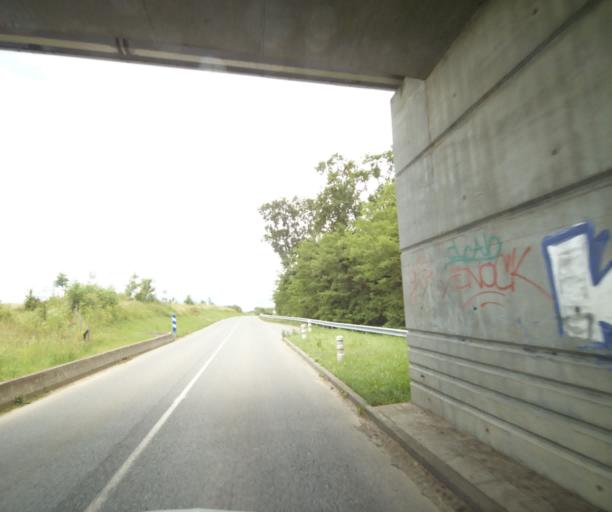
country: FR
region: Rhone-Alpes
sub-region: Departement de la Haute-Savoie
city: Allinges
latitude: 46.3471
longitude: 6.4530
